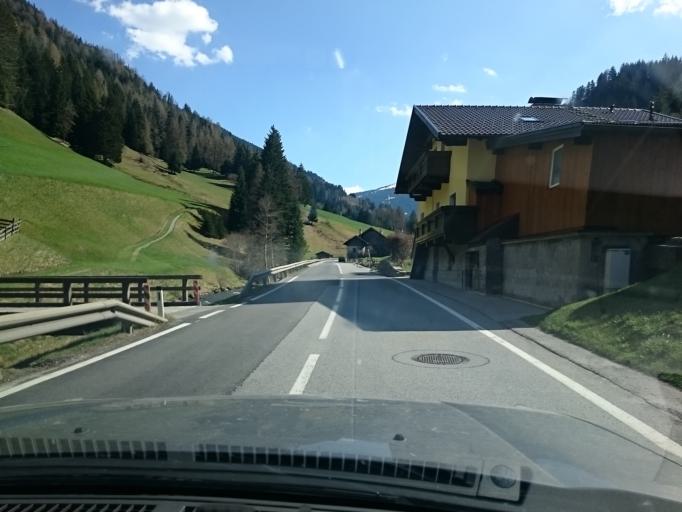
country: AT
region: Tyrol
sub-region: Politischer Bezirk Innsbruck Land
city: Gries am Brenner
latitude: 47.0585
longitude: 11.4853
